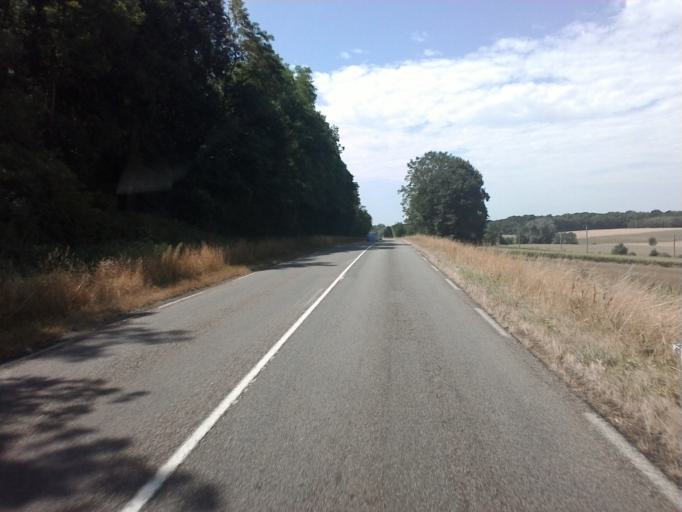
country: FR
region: Franche-Comte
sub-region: Departement du Jura
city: Cousance
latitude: 46.5902
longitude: 5.4495
